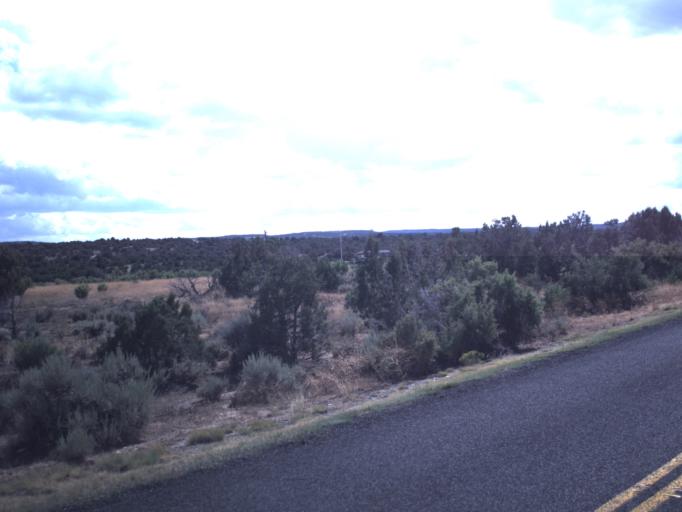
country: US
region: Utah
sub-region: Duchesne County
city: Duchesne
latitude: 40.1796
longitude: -110.4513
